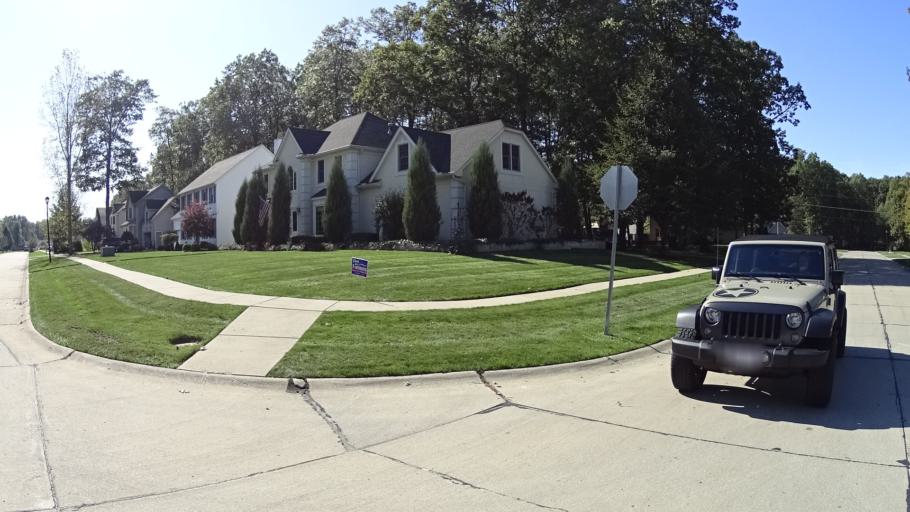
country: US
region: Ohio
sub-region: Lorain County
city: Vermilion-on-the-Lake
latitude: 41.4218
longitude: -82.3319
